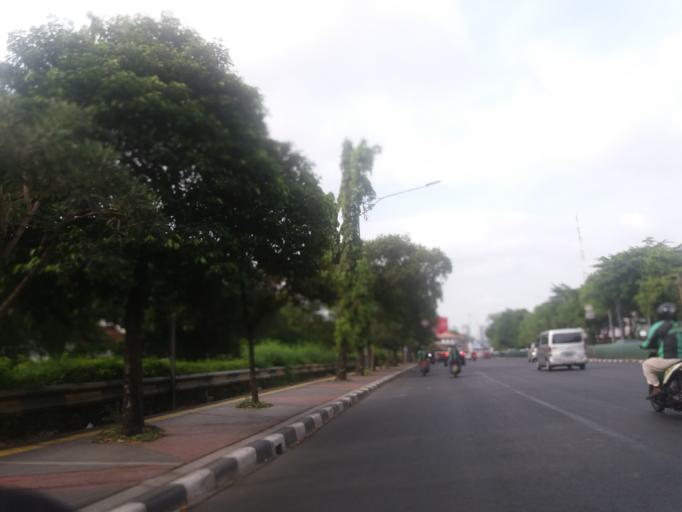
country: ID
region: Jakarta Raya
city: Jakarta
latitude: -6.1649
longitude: 106.8365
